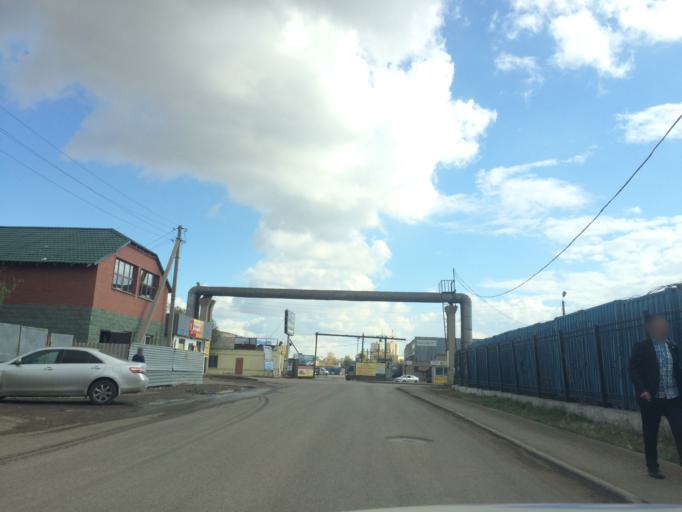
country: KZ
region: Astana Qalasy
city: Astana
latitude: 51.1827
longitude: 71.3851
